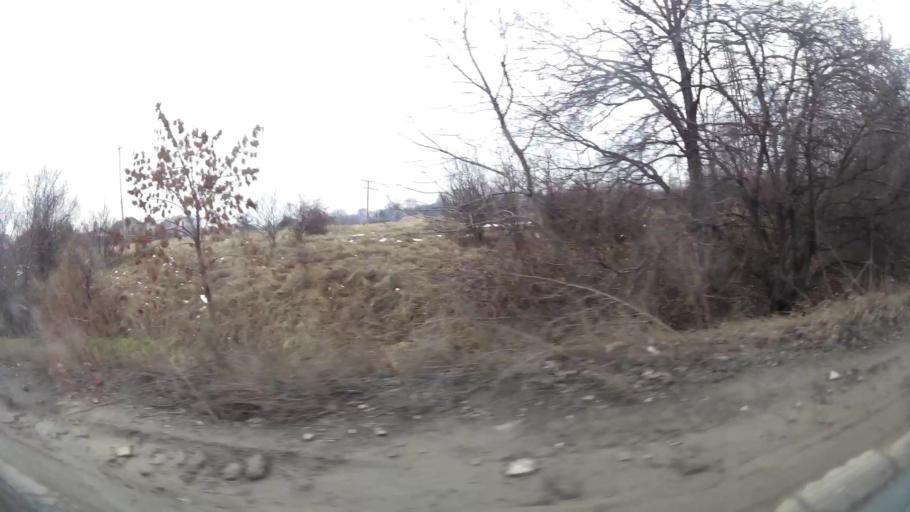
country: BG
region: Sofiya
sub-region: Obshtina Bozhurishte
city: Bozhurishte
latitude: 42.6997
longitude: 23.2303
